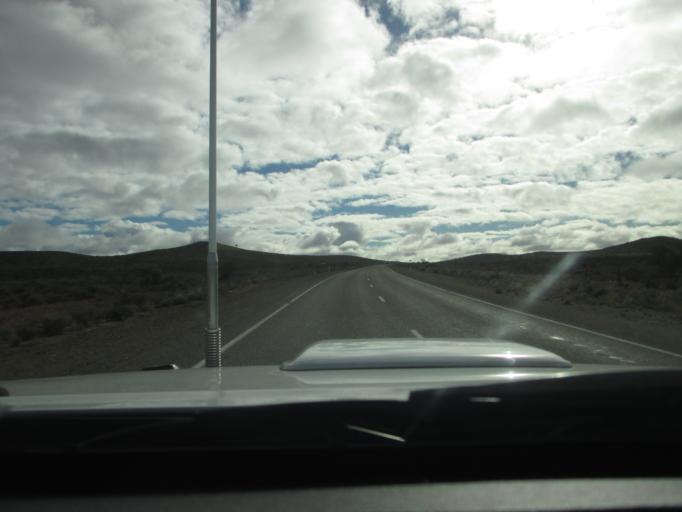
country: AU
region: South Australia
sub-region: Flinders Ranges
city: Quorn
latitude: -32.2750
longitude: 138.4959
